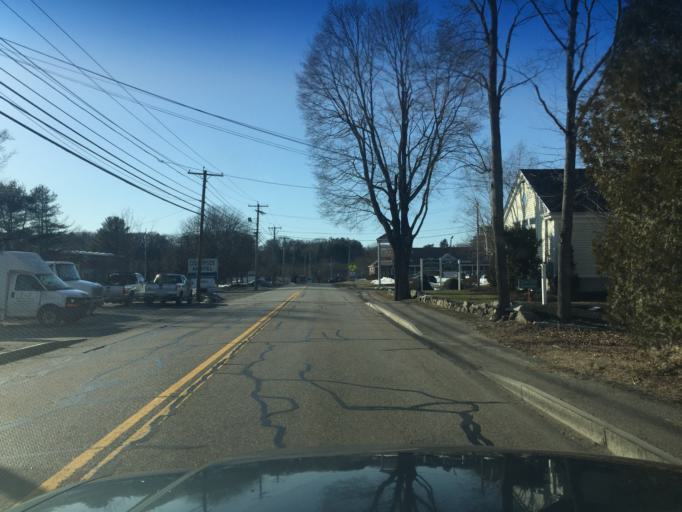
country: US
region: Massachusetts
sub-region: Norfolk County
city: Bellingham
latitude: 42.0820
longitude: -71.4656
